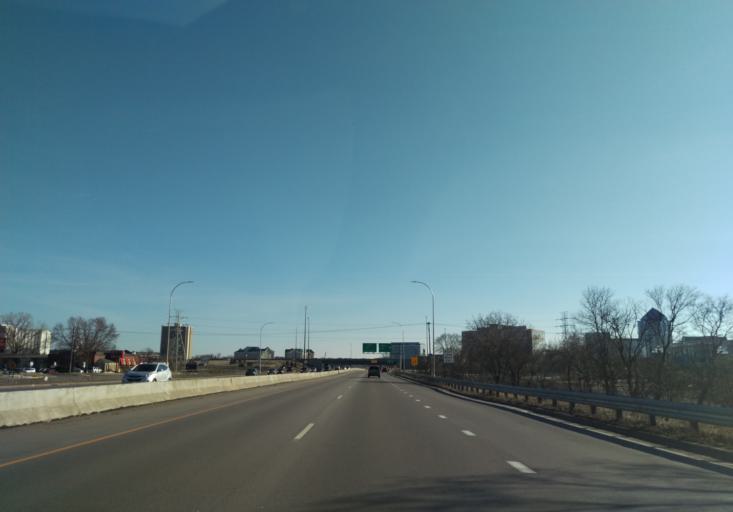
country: US
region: Minnesota
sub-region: Hennepin County
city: Edina
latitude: 44.8631
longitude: -93.3503
